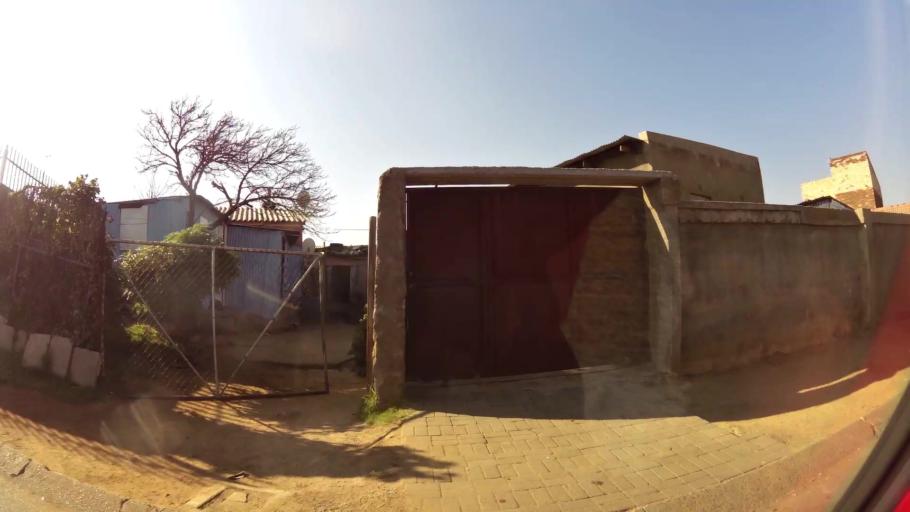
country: ZA
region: Gauteng
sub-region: City of Johannesburg Metropolitan Municipality
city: Soweto
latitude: -26.2502
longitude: 27.9499
